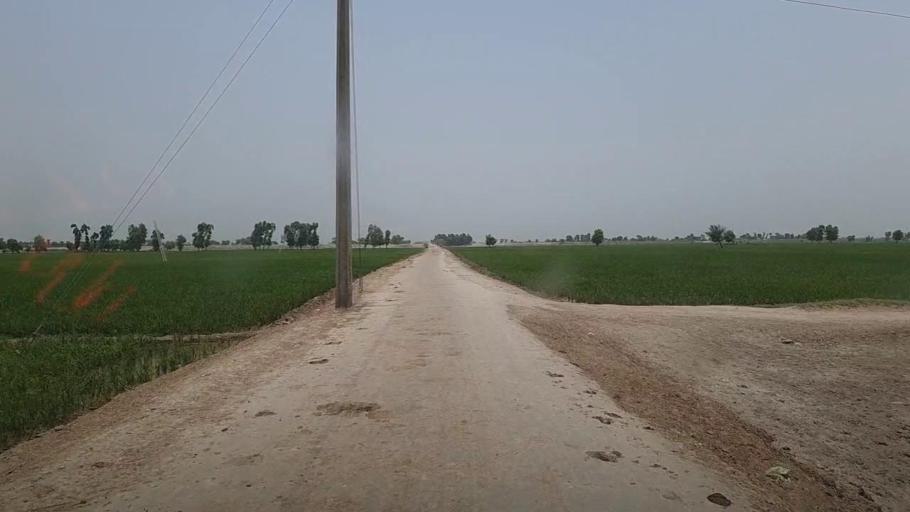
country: PK
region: Sindh
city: Sita Road
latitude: 27.0446
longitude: 67.8467
